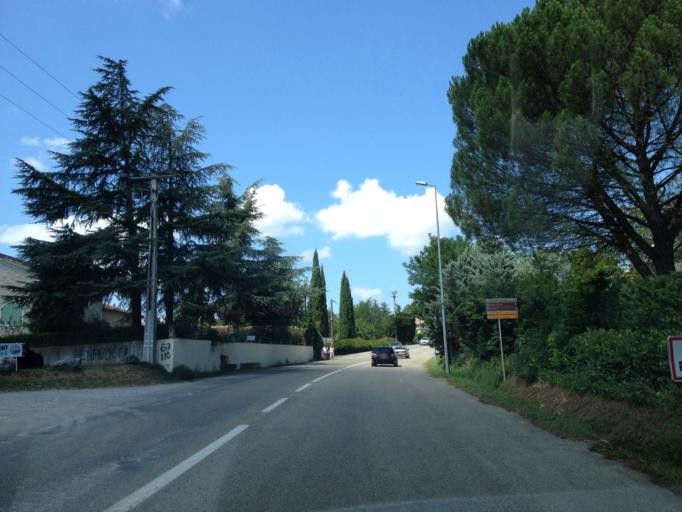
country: FR
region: Rhone-Alpes
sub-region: Departement de l'Ardeche
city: Ruoms
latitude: 44.3993
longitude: 4.3899
